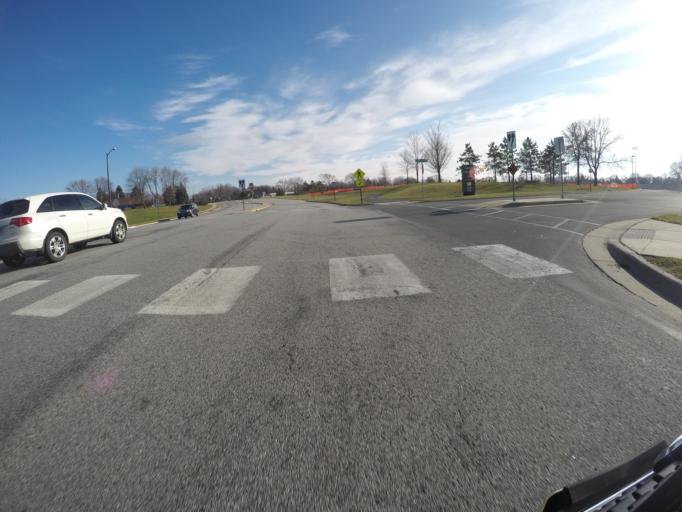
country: US
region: Minnesota
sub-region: Hennepin County
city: Eden Prairie
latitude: 44.8694
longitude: -93.4883
